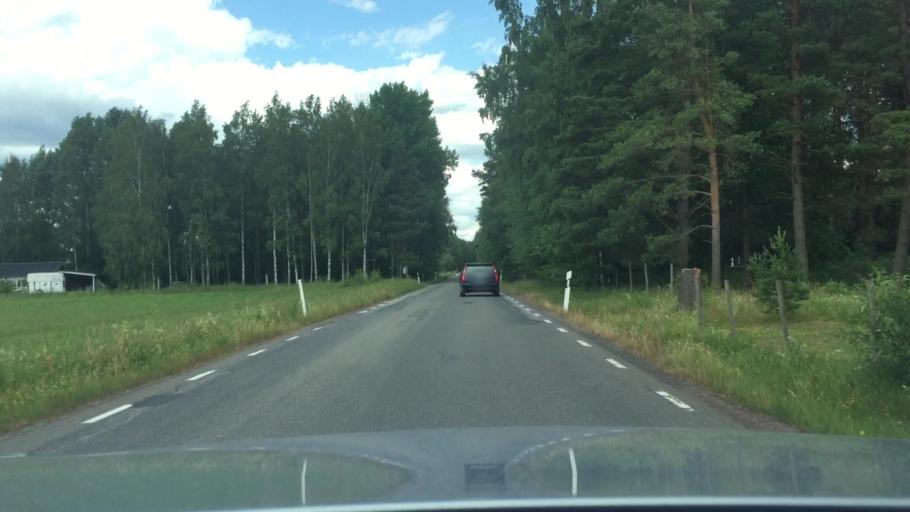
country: SE
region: Vaestra Goetaland
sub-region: Tidaholms Kommun
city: Tidaholm
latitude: 58.1973
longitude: 13.9787
